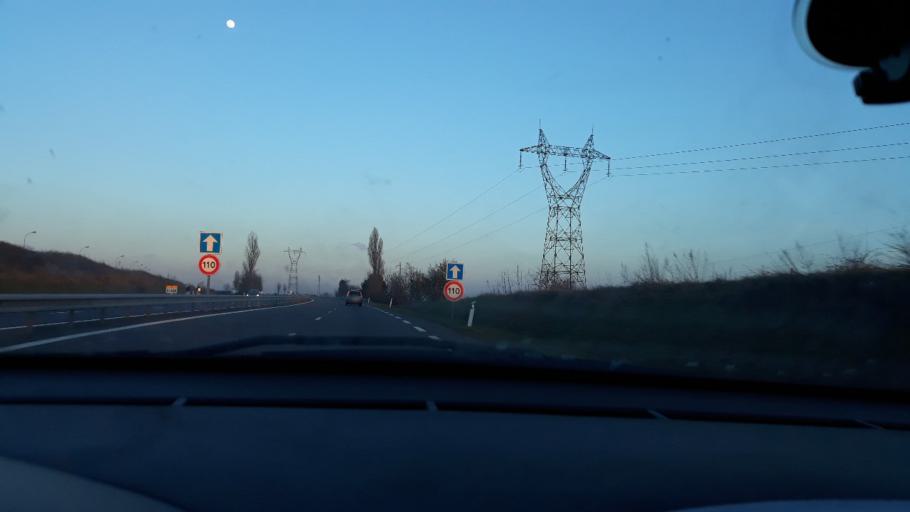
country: FR
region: Lorraine
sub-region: Departement de la Moselle
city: OEting
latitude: 49.1608
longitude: 6.9254
